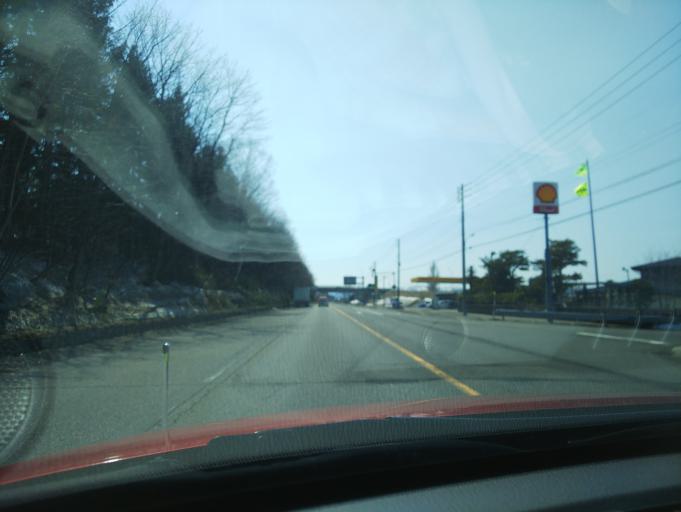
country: JP
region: Hokkaido
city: Nayoro
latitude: 44.3012
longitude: 142.4313
